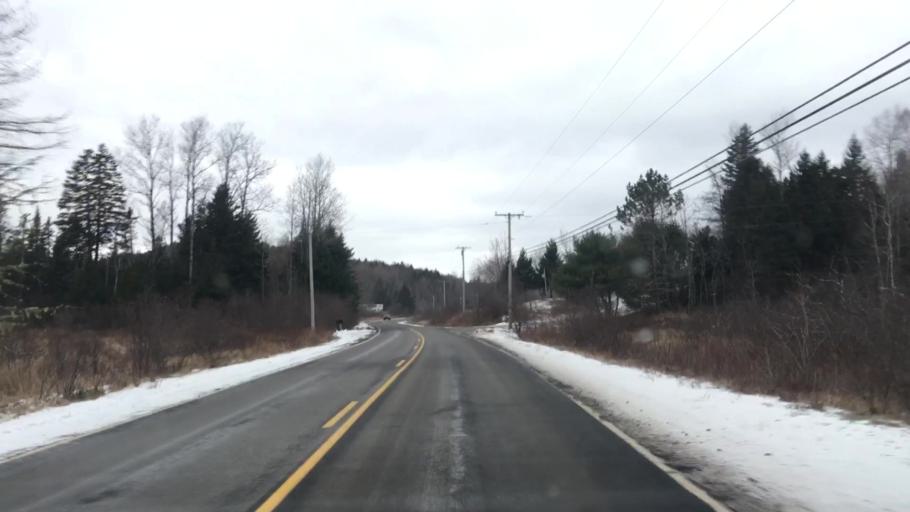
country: US
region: Maine
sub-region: Washington County
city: Machiasport
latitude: 44.7079
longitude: -67.3645
